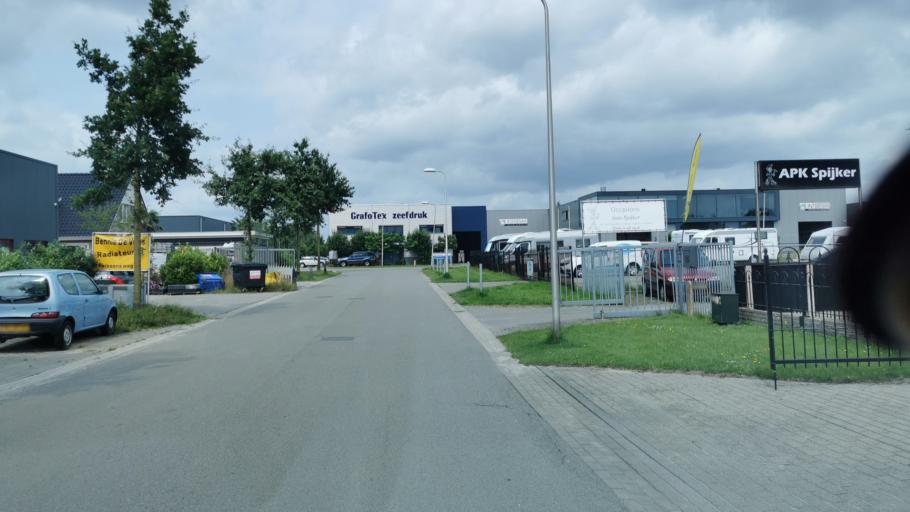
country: NL
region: Overijssel
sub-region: Gemeente Enschede
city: Enschede
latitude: 52.2256
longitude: 6.9505
